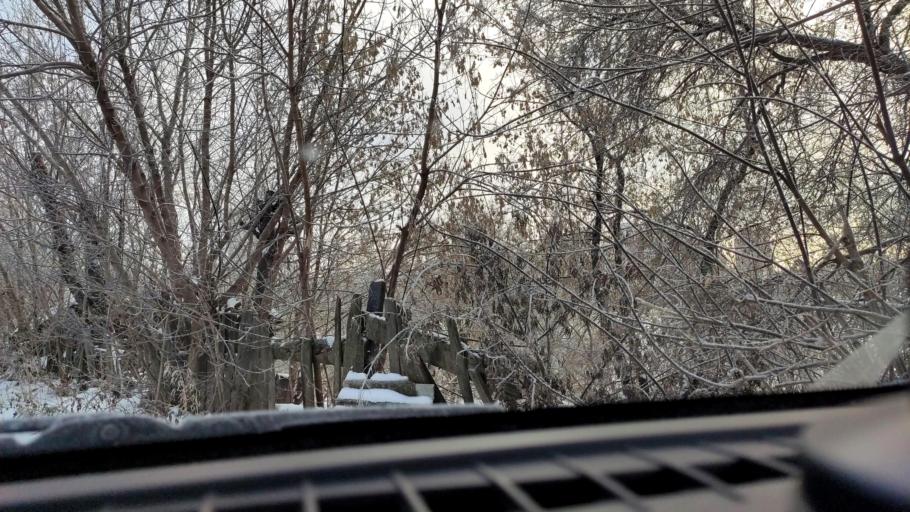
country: RU
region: Perm
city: Kondratovo
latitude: 57.9962
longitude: 56.1258
